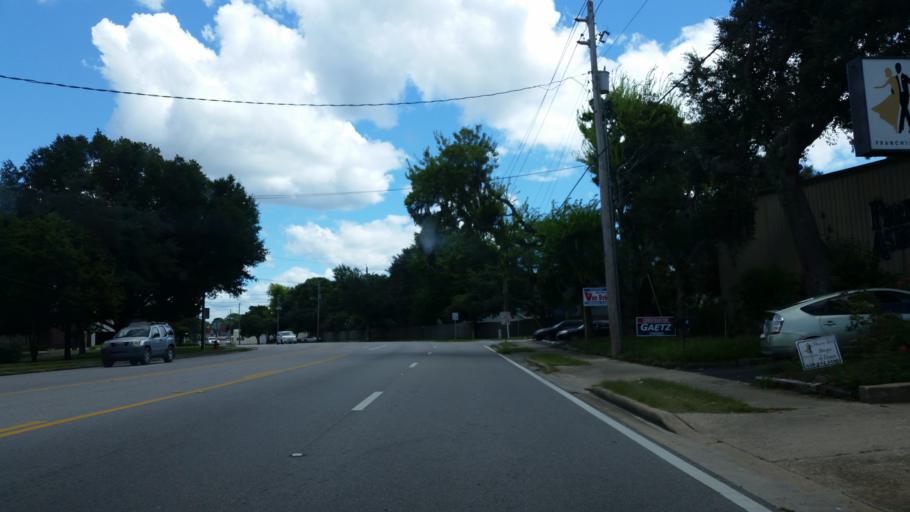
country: US
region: Florida
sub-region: Okaloosa County
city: Fort Walton Beach
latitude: 30.4229
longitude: -86.6132
